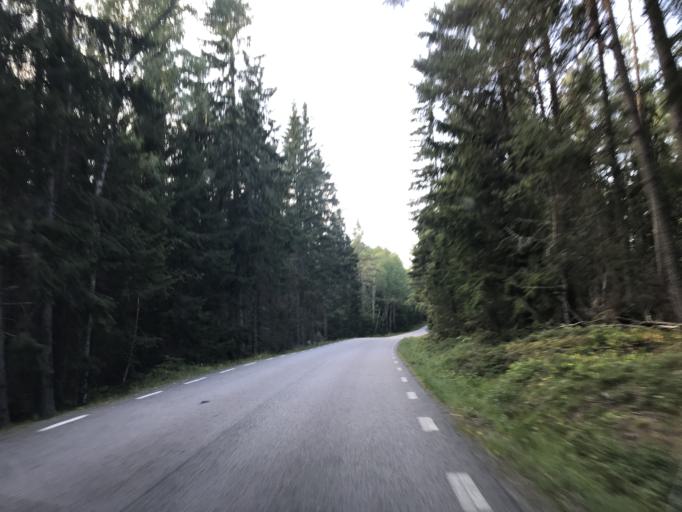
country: SE
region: Stockholm
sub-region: Norrtalje Kommun
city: Bjorko
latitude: 59.8759
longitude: 19.0092
